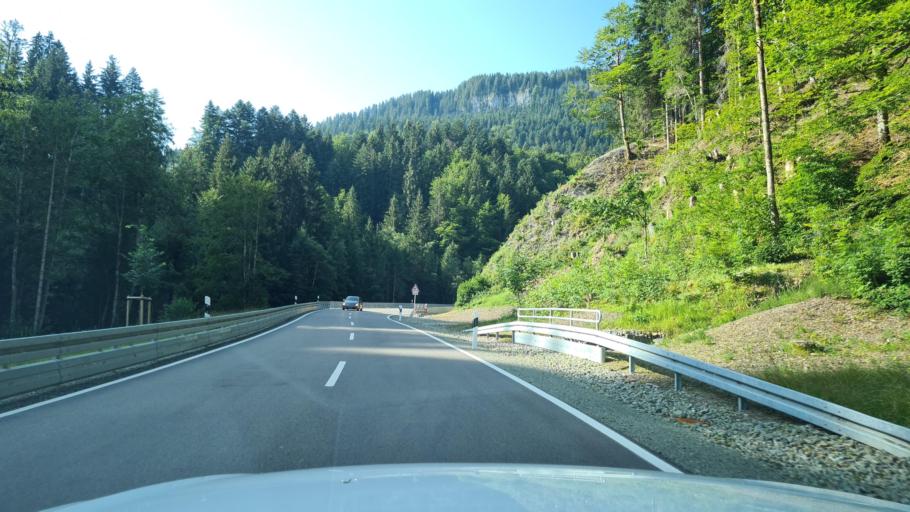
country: DE
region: Bavaria
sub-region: Swabia
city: Obermaiselstein
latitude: 47.4428
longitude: 10.2296
